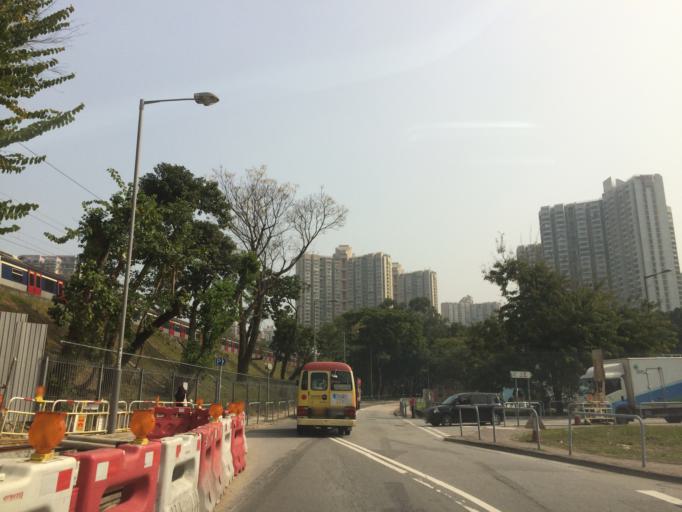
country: HK
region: Tai Po
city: Tai Po
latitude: 22.4537
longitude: 114.1568
